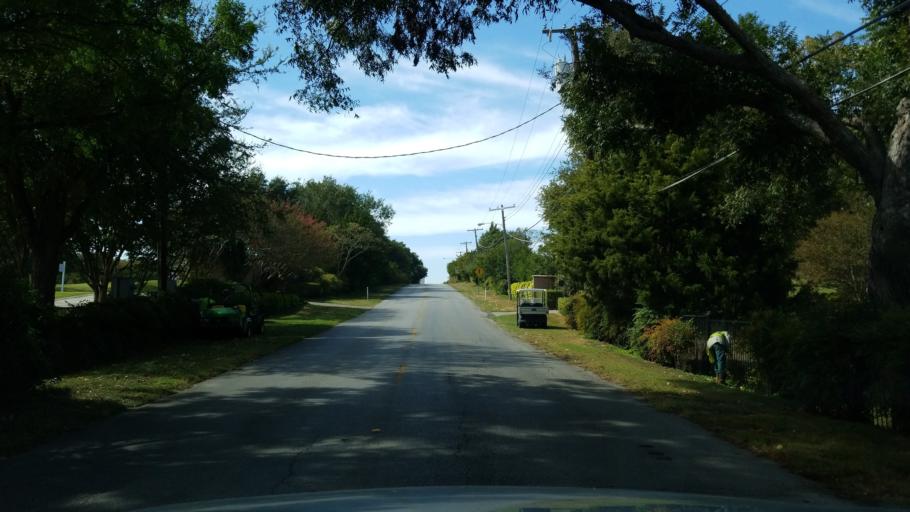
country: US
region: Texas
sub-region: Dallas County
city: Highland Park
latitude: 32.8118
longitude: -96.7442
